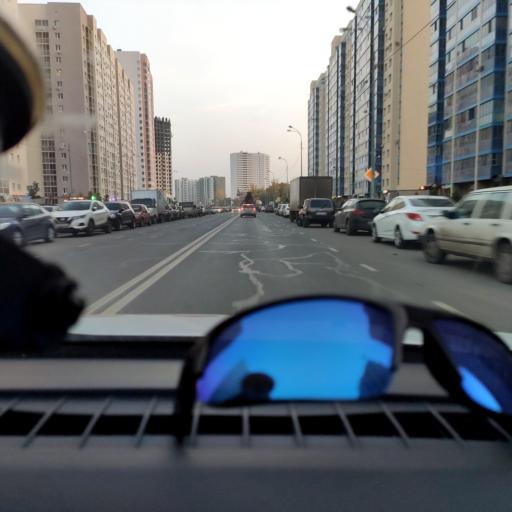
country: RU
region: Samara
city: Rozhdestveno
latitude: 53.1517
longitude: 50.0748
